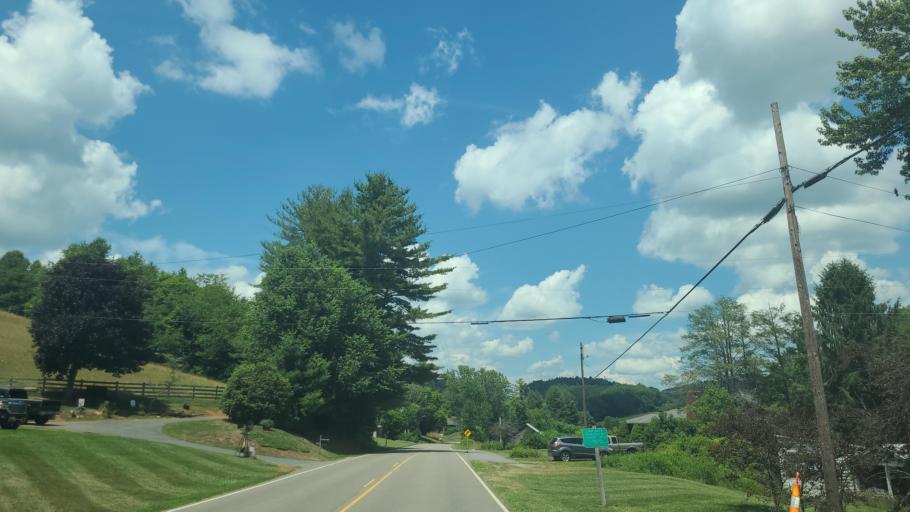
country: US
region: North Carolina
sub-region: Watauga County
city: Boone
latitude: 36.2379
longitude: -81.5449
